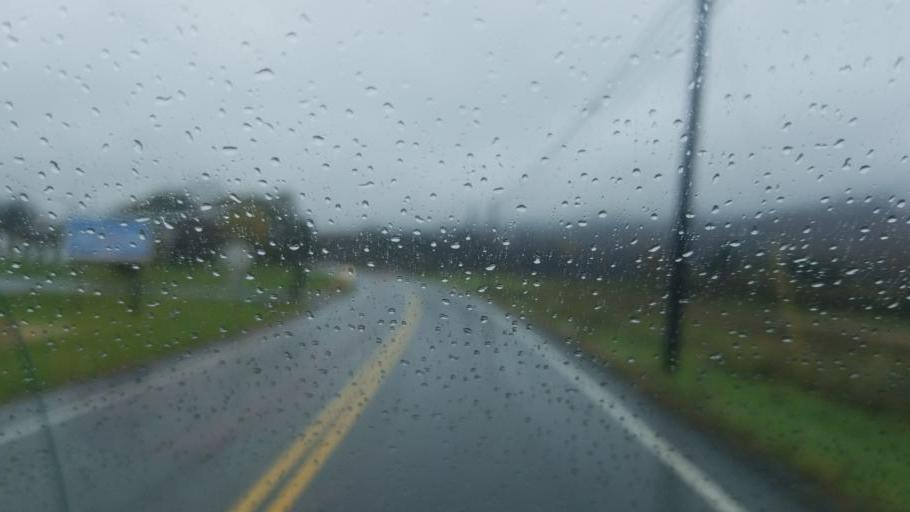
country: US
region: Pennsylvania
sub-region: Clinton County
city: Mill Hall
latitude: 41.0755
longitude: -77.5688
